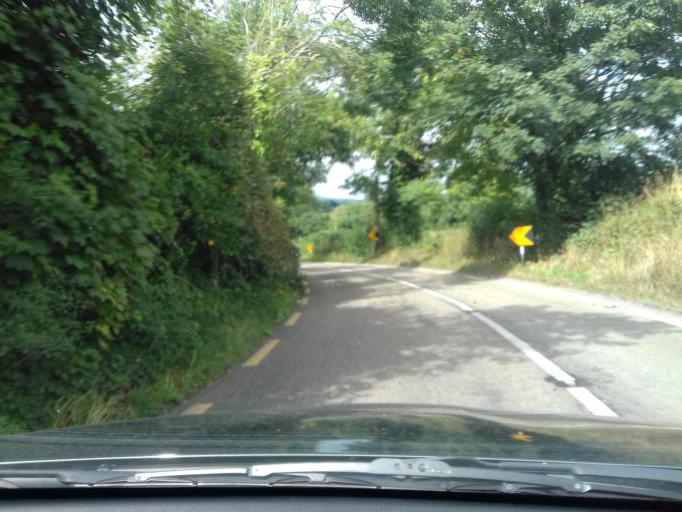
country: IE
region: Leinster
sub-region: County Carlow
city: Tullow
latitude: 52.8593
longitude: -6.7055
